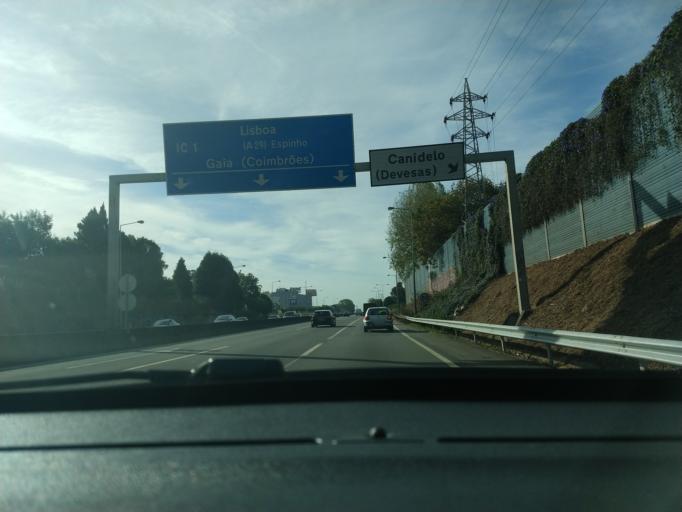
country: PT
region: Porto
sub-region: Vila Nova de Gaia
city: Canidelo
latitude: 41.1300
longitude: -8.6357
